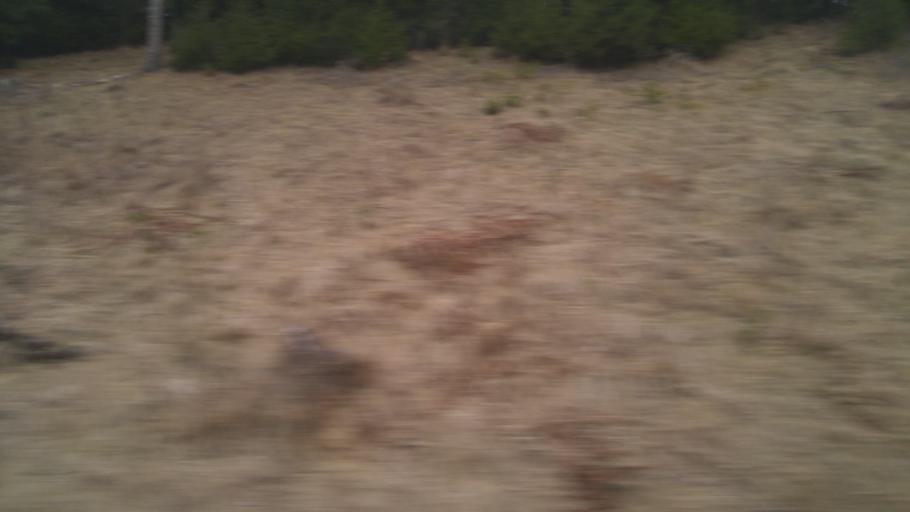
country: NO
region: Akershus
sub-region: Eidsvoll
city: Eidsvoll
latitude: 60.3726
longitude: 11.2427
